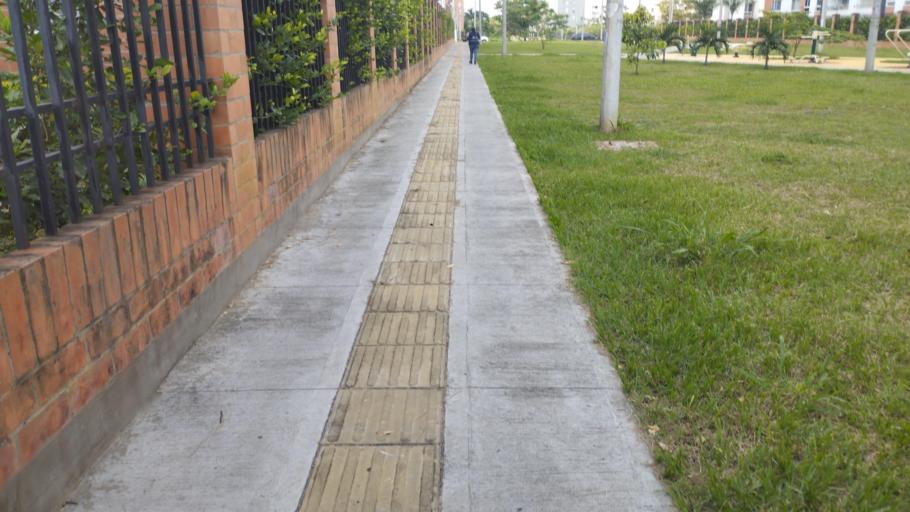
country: CO
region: Valle del Cauca
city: Cali
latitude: 3.3697
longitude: -76.5153
